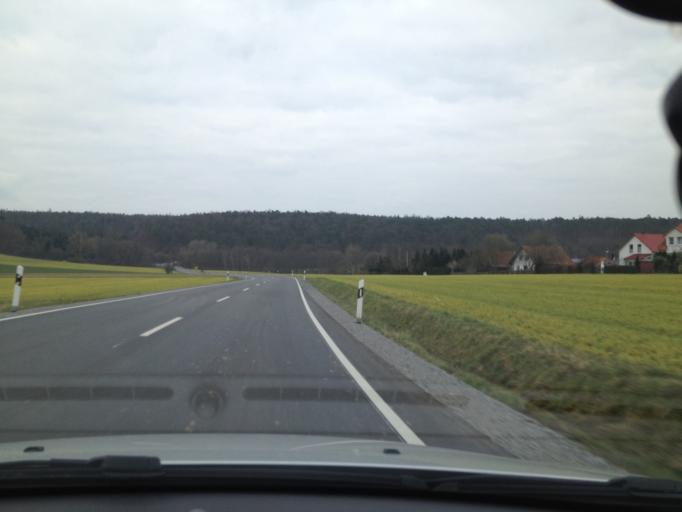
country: DE
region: Bavaria
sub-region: Regierungsbezirk Unterfranken
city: Kreuzwertheim
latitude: 49.7790
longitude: 9.5376
